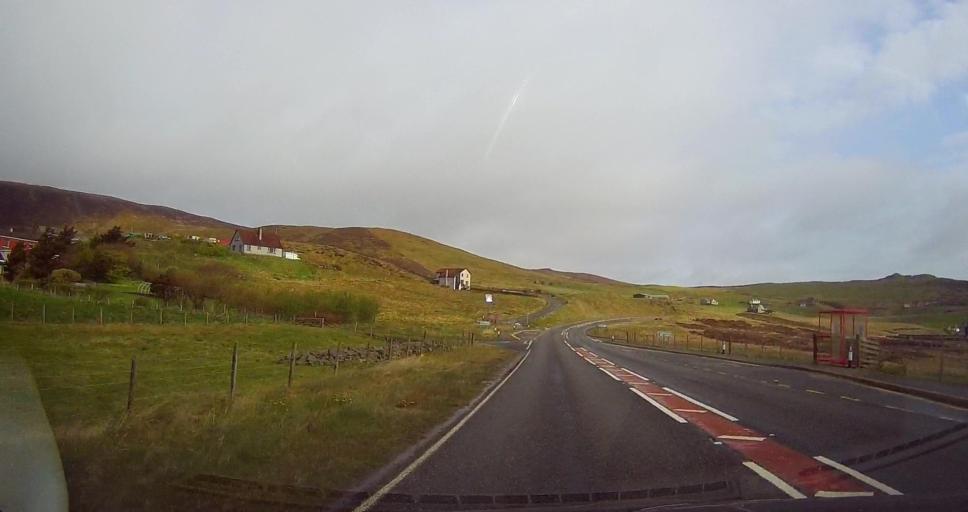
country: GB
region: Scotland
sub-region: Shetland Islands
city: Sandwick
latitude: 60.0991
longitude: -1.2339
